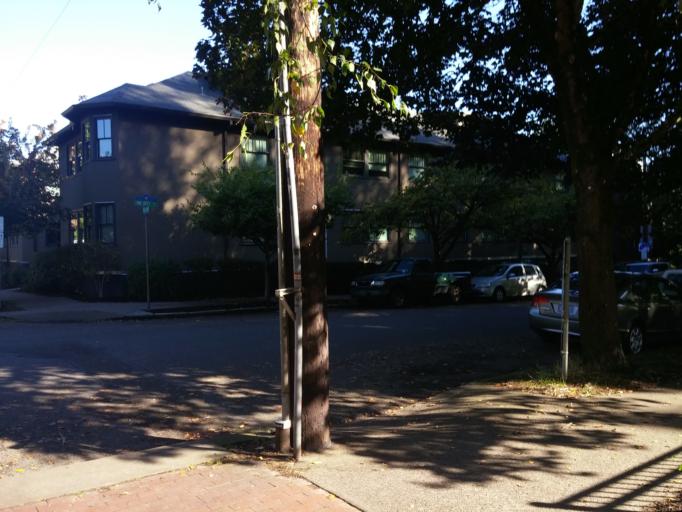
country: US
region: Oregon
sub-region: Multnomah County
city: Portland
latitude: 45.5269
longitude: -122.6922
